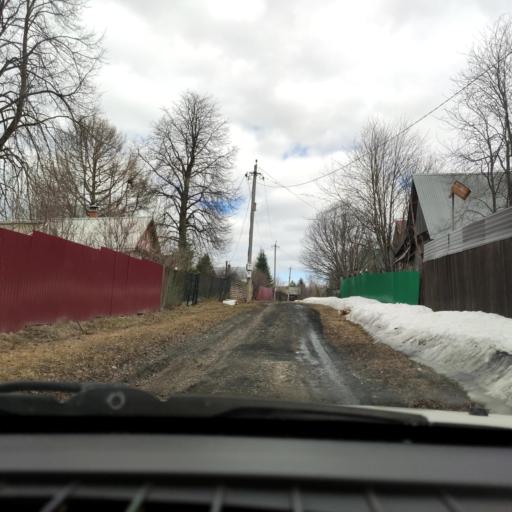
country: RU
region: Perm
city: Novyye Lyady
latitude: 58.1732
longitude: 56.5973
